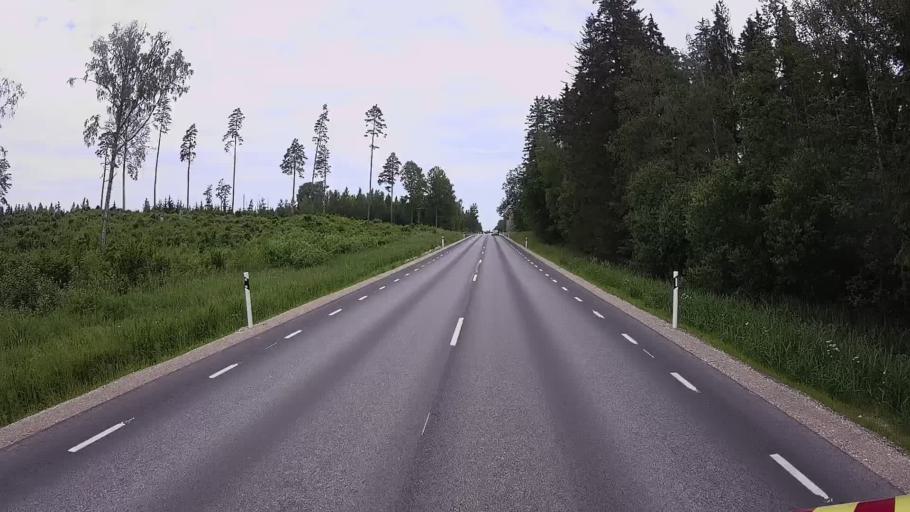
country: EE
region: Viljandimaa
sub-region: Viljandi linn
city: Viljandi
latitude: 58.2560
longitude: 25.5892
